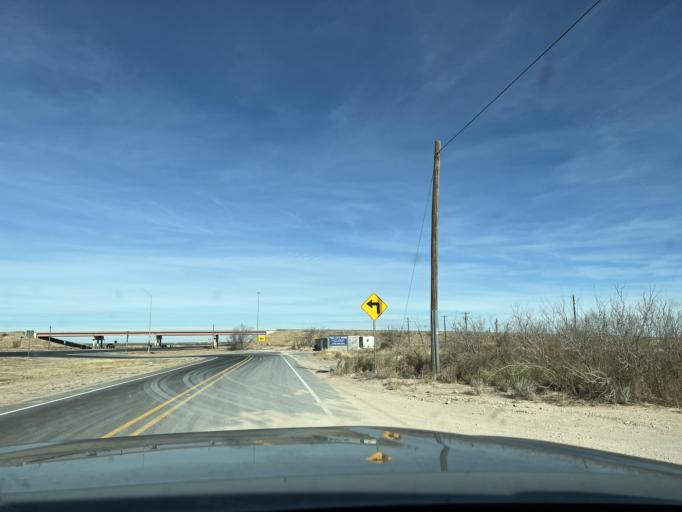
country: US
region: Texas
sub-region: Ector County
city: Gardendale
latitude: 32.0217
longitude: -102.4292
